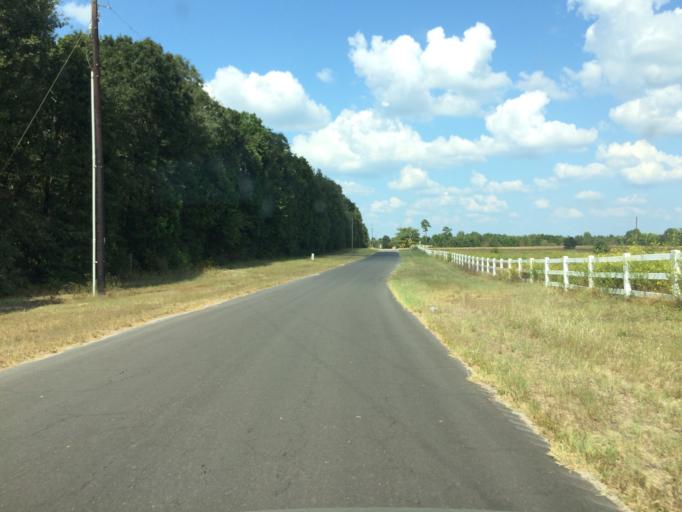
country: US
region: Texas
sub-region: Wood County
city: Hawkins
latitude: 32.6648
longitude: -95.2049
